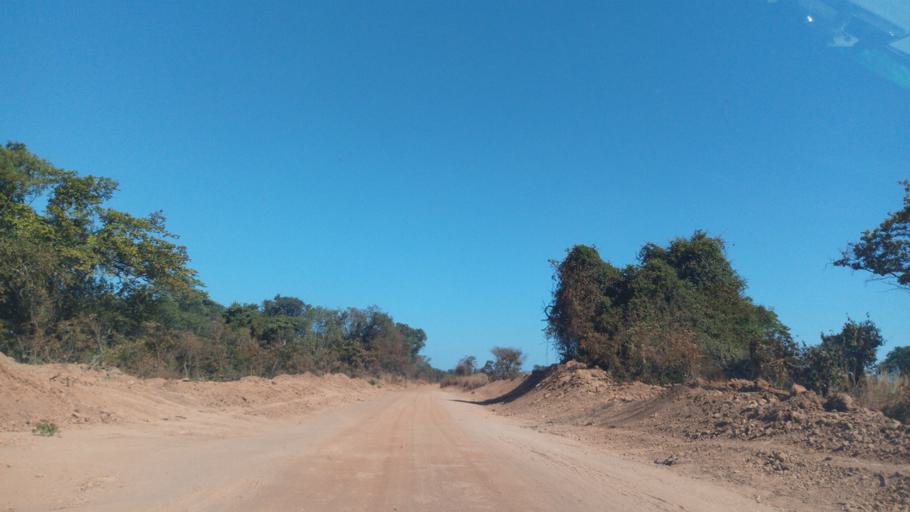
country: ZM
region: Luapula
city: Mwense
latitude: -10.7548
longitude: 28.3188
